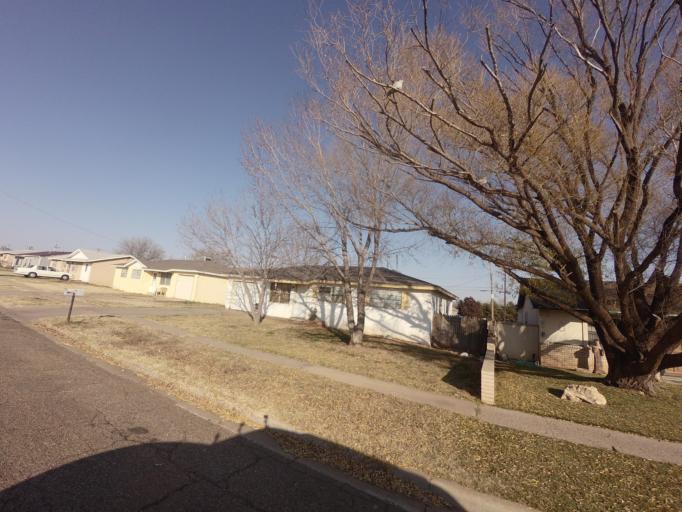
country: US
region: New Mexico
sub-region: Curry County
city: Clovis
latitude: 34.4184
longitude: -103.2104
